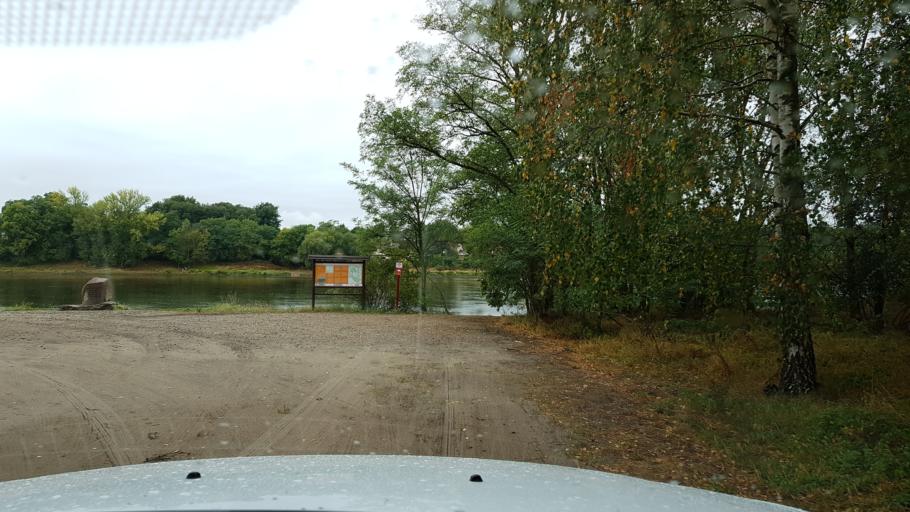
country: DE
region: Brandenburg
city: Oderberg
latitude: 52.8394
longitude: 14.1250
